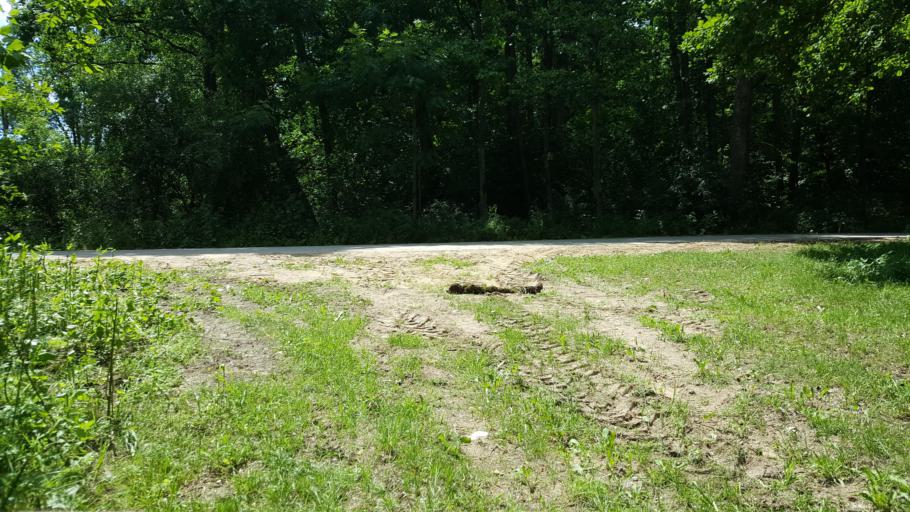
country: BY
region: Brest
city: Kamyanyuki
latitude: 52.5788
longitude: 23.7358
